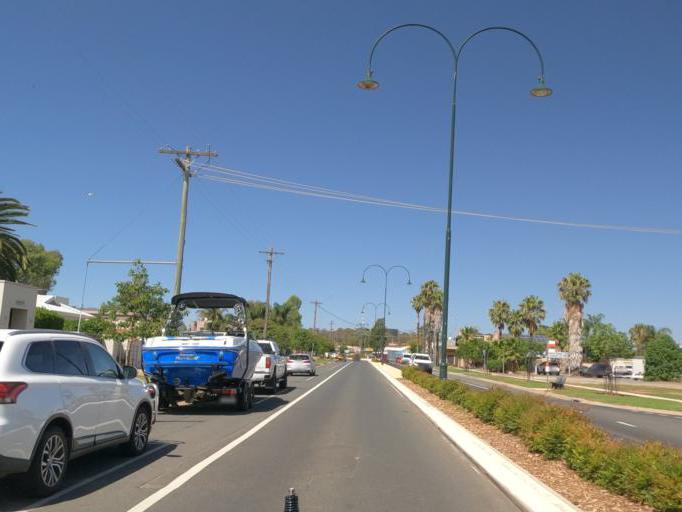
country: AU
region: New South Wales
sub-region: Corowa Shire
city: Mulwala
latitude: -35.9910
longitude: 146.0037
